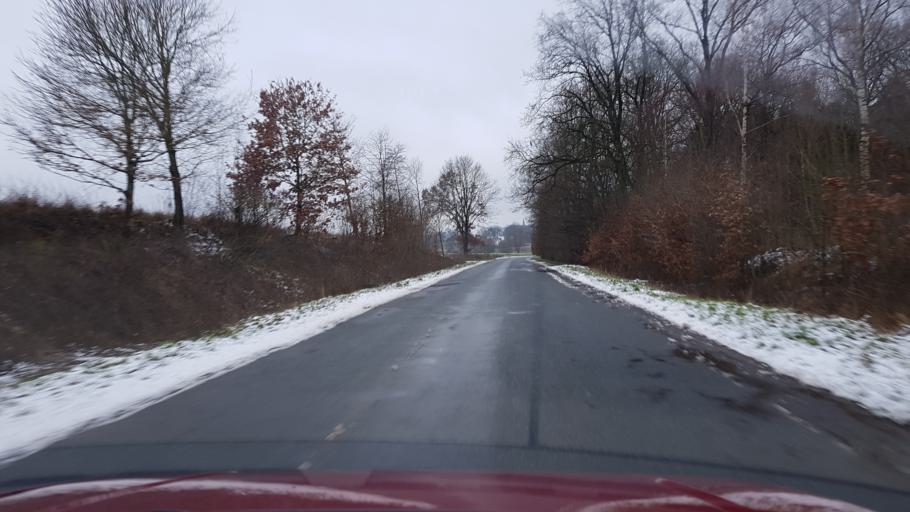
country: PL
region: West Pomeranian Voivodeship
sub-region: Powiat goleniowski
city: Nowogard
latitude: 53.6680
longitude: 15.1945
